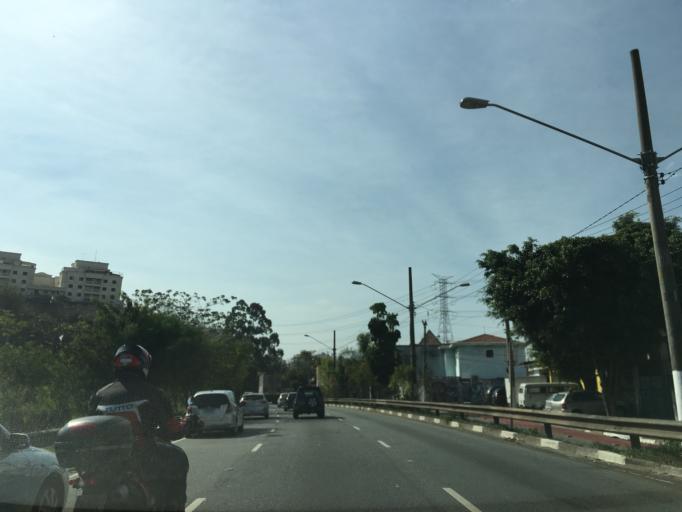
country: BR
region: Sao Paulo
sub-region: Osasco
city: Osasco
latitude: -23.5673
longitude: -46.7563
